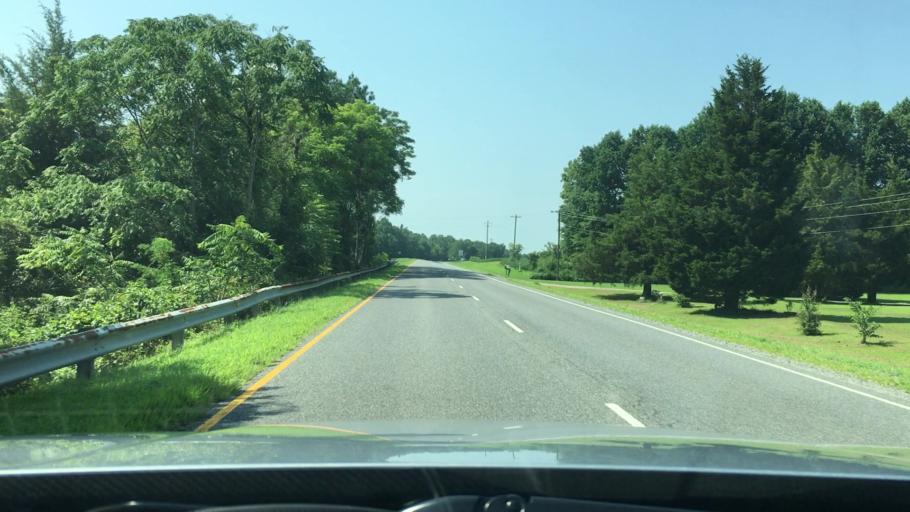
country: US
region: Virginia
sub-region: Caroline County
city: Bowling Green
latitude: 37.9885
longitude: -77.4182
